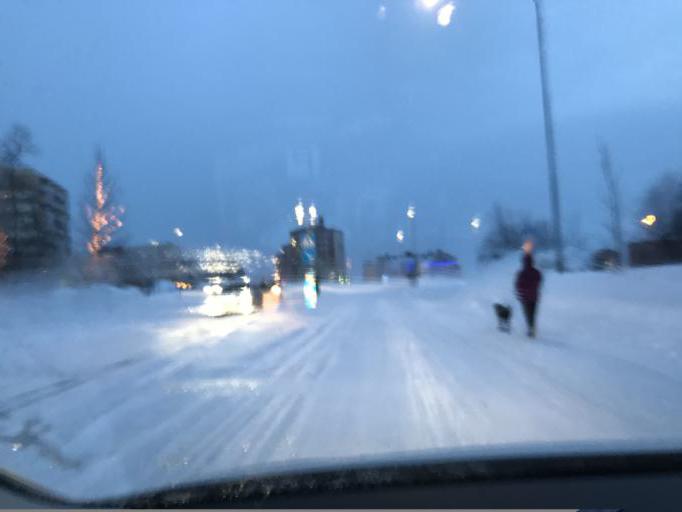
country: SE
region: Norrbotten
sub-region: Kiruna Kommun
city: Kiruna
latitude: 67.8600
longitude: 20.2248
